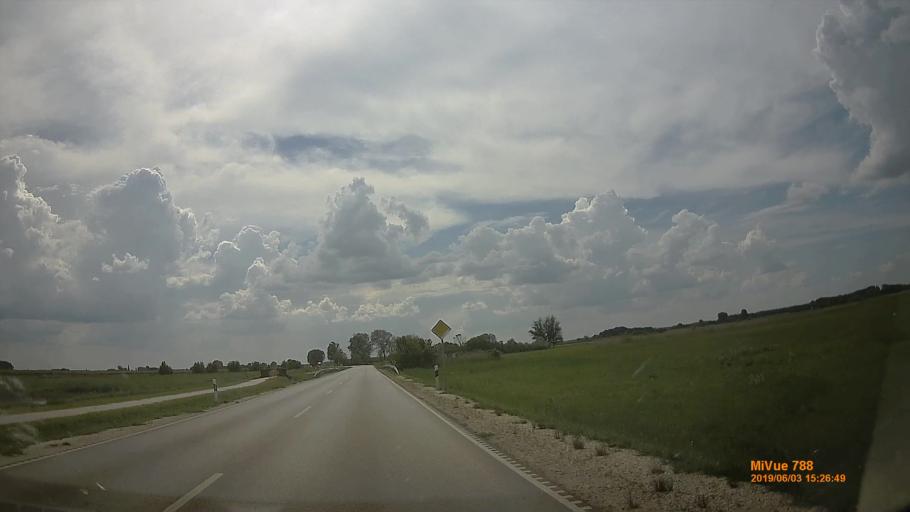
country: HU
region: Bacs-Kiskun
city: Soltvadkert
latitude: 46.6019
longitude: 19.4377
